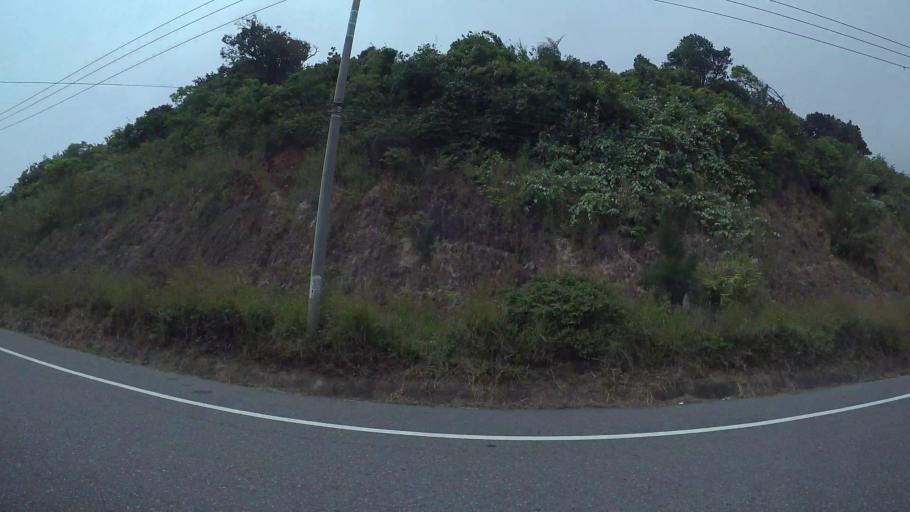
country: VN
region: Da Nang
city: Son Tra
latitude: 16.1009
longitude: 108.3078
